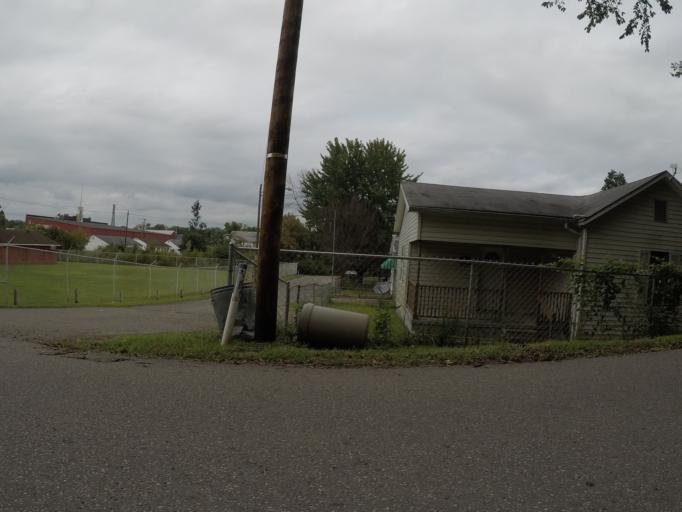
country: US
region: West Virginia
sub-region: Cabell County
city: Pea Ridge
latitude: 38.4269
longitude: -82.3805
